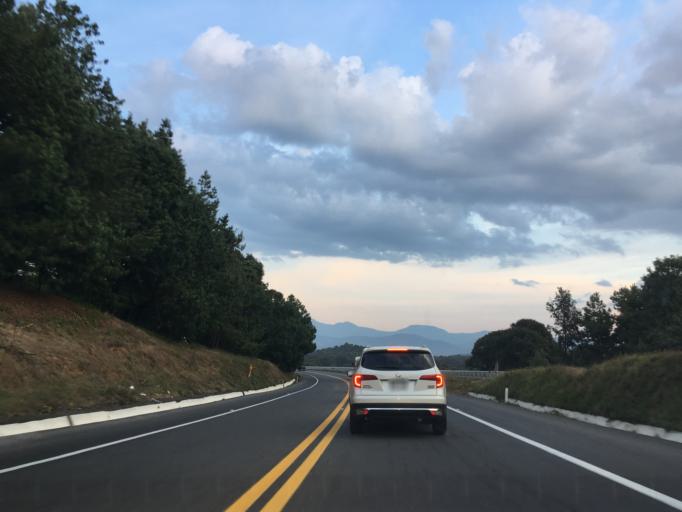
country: MX
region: Michoacan
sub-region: Patzcuaro
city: Colonia Vista Bella (Lomas del Peaje)
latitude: 19.5082
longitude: -101.5745
